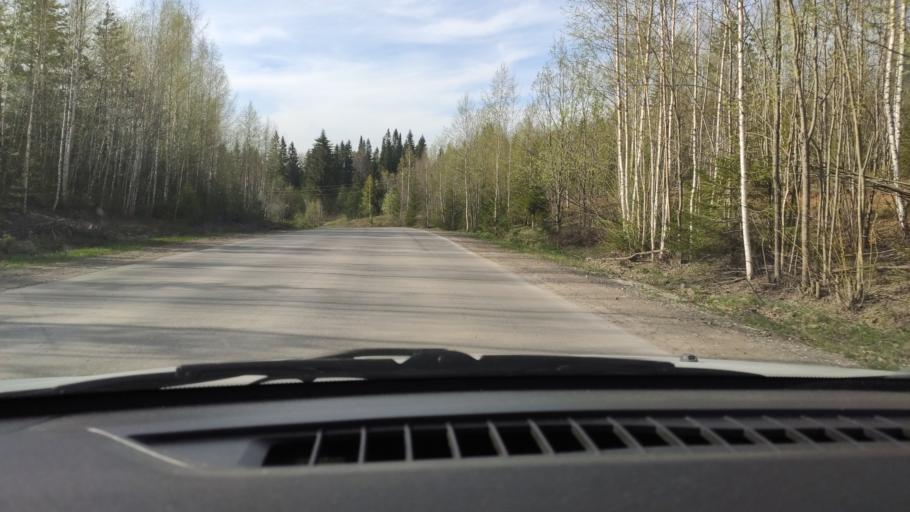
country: RU
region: Perm
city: Novyye Lyady
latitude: 57.9306
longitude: 56.6431
